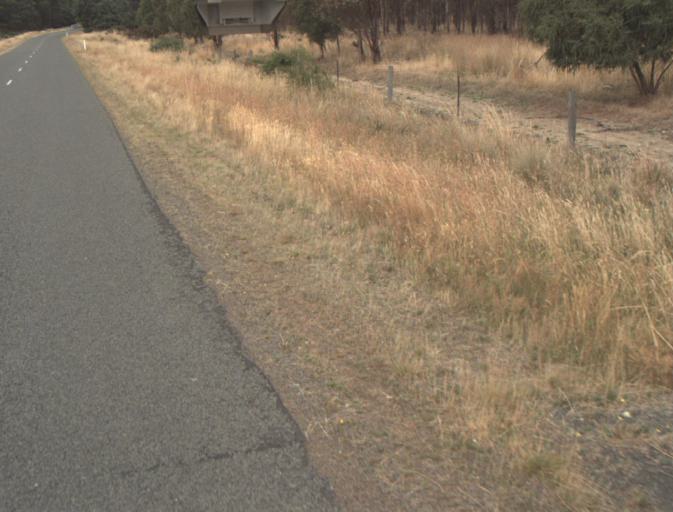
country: AU
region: Tasmania
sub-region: Northern Midlands
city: Evandale
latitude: -41.4867
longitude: 147.5030
